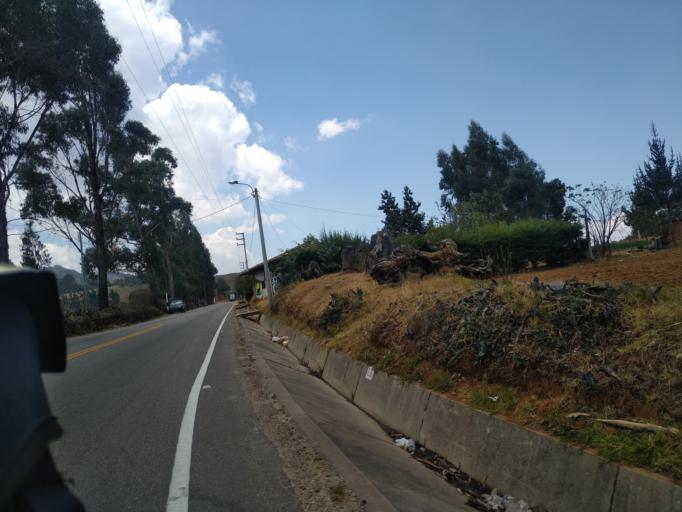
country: PE
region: Cajamarca
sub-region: San Marcos
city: San Marcos
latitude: -7.2831
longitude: -78.2216
